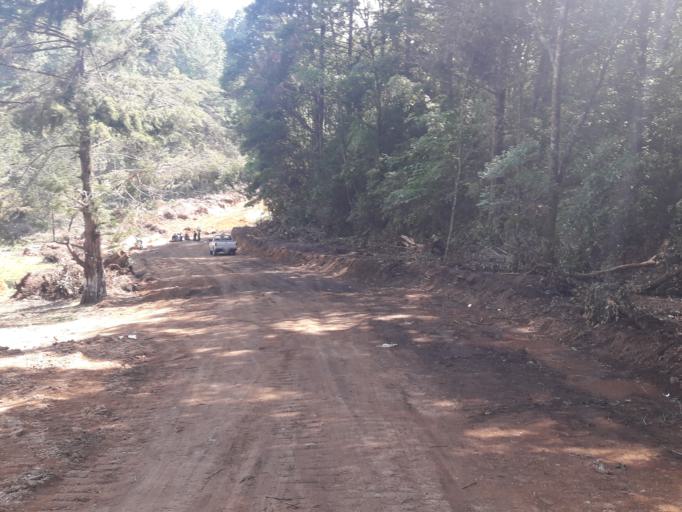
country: GT
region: Quiche
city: Nebaj
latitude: 15.4273
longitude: -91.1362
